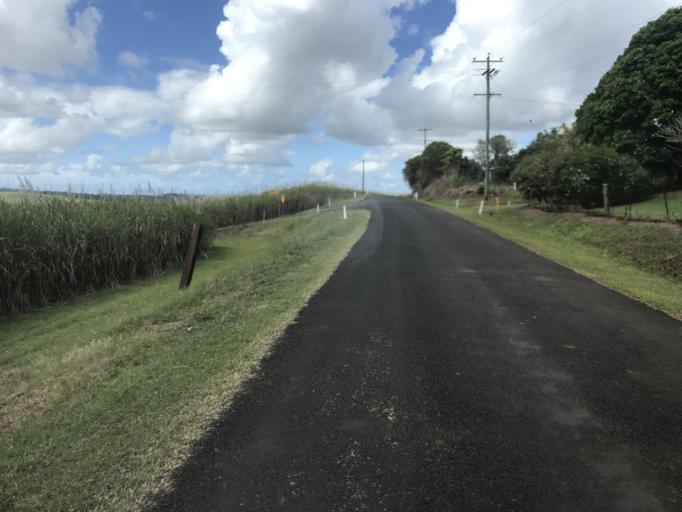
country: AU
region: Queensland
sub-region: Cassowary Coast
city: Innisfail
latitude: -17.5536
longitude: 145.8903
